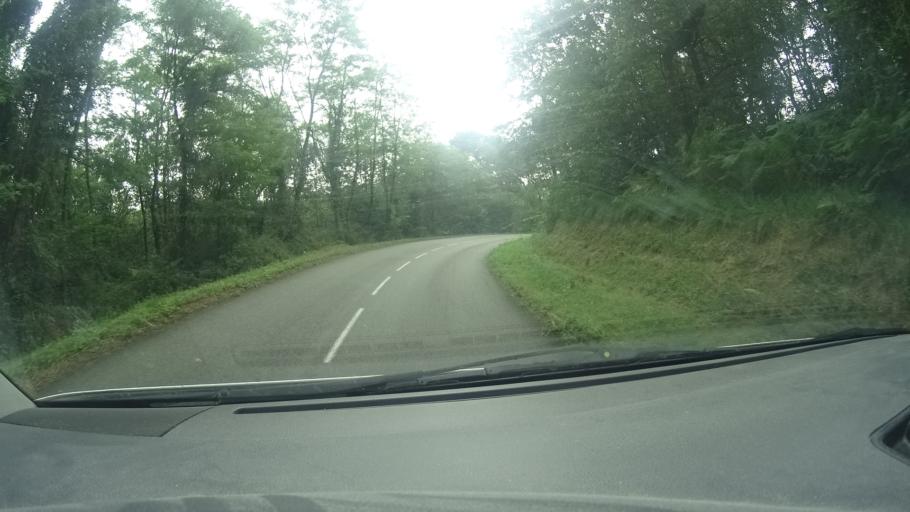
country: FR
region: Aquitaine
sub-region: Departement des Pyrenees-Atlantiques
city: Mont
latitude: 43.4883
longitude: -0.6888
